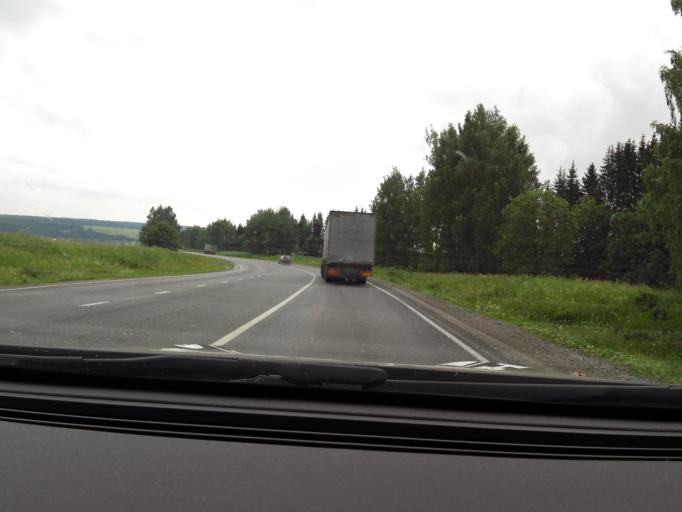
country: RU
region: Perm
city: Suksun
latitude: 57.0753
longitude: 57.4101
